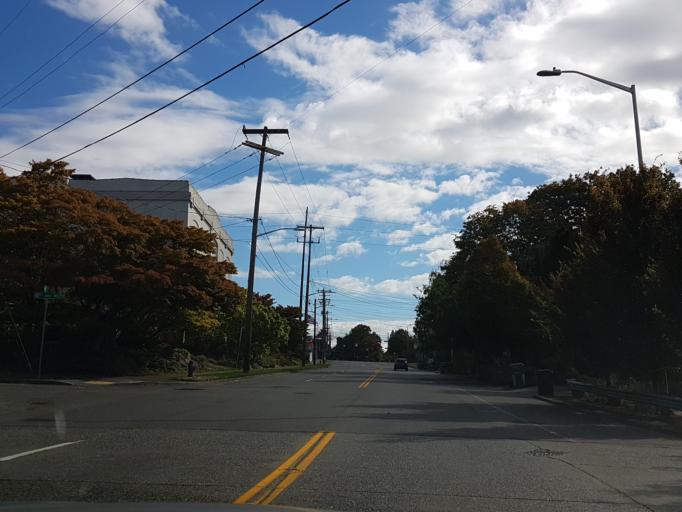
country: US
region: Washington
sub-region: King County
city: Shoreline
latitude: 47.6831
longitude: -122.3206
